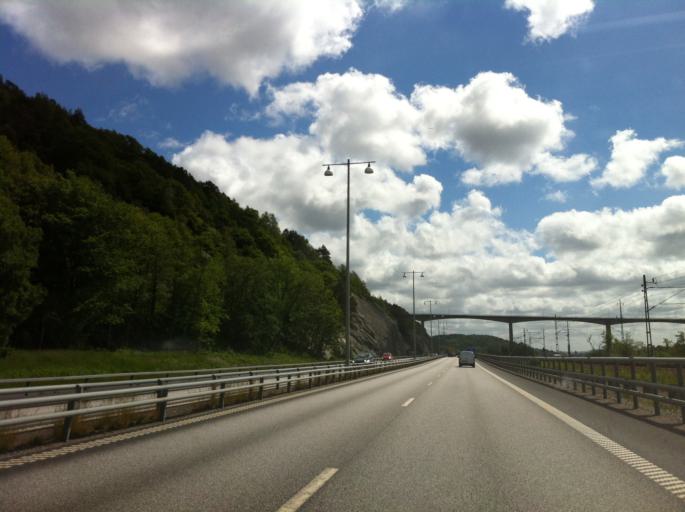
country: SE
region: Vaestra Goetaland
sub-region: Ale Kommun
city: Surte
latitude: 57.8498
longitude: 12.0138
